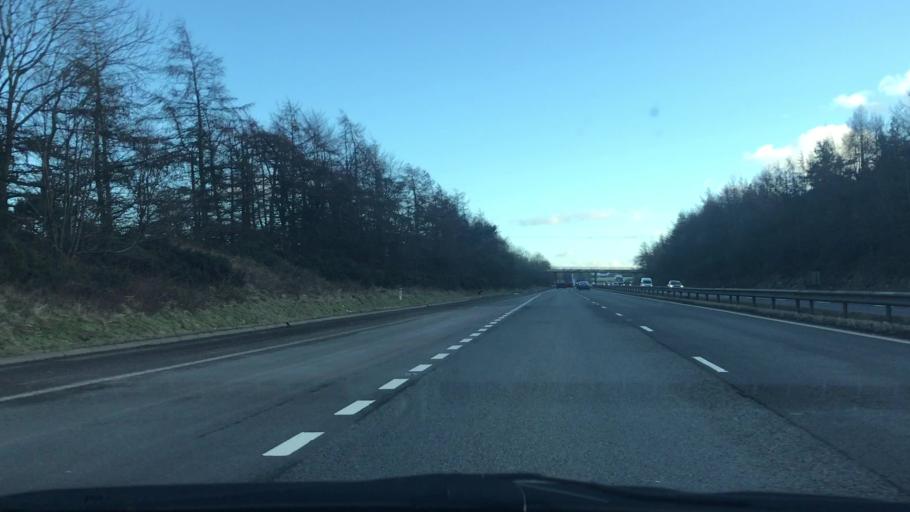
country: GB
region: Scotland
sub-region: South Lanarkshire
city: Larkhall
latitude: 55.7083
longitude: -3.9523
